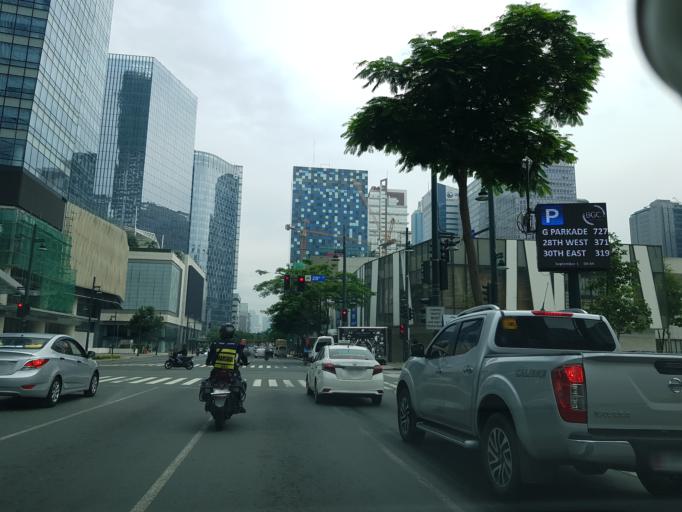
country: PH
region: Metro Manila
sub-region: Makati City
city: Makati City
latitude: 14.5503
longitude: 121.0473
